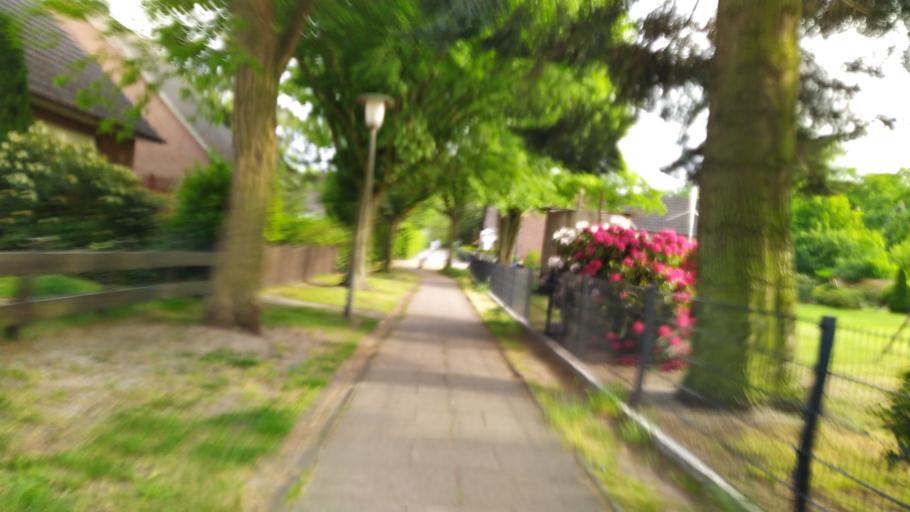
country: DE
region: Hamburg
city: Altona
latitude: 53.4784
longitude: 9.8946
